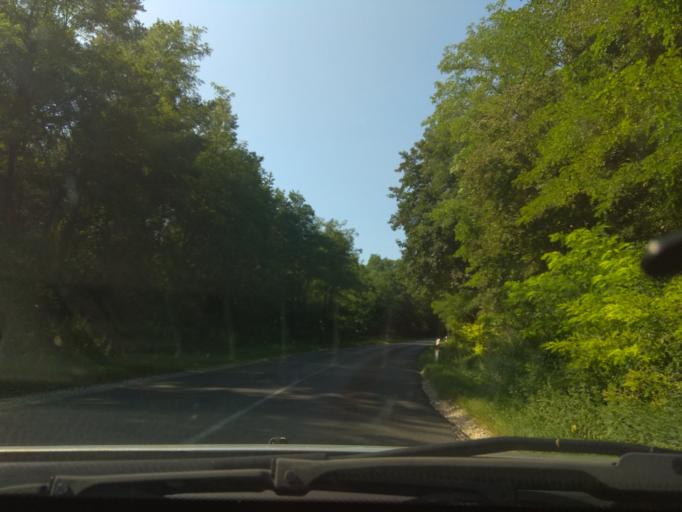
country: HU
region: Borsod-Abauj-Zemplen
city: Harsany
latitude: 47.9913
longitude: 20.7541
